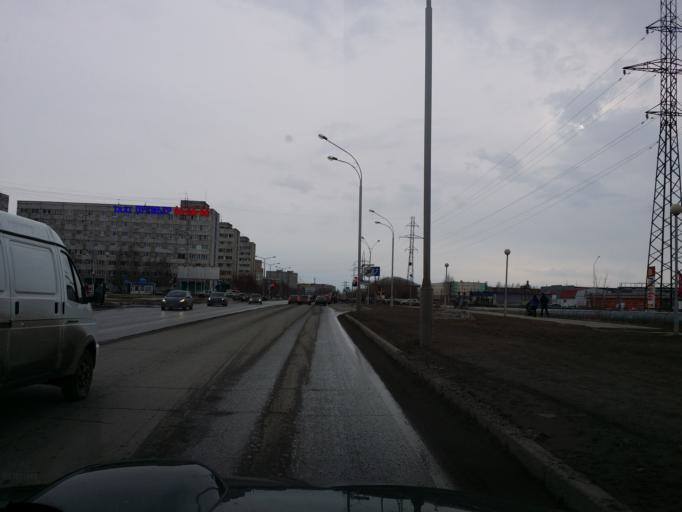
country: RU
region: Khanty-Mansiyskiy Avtonomnyy Okrug
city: Nizhnevartovsk
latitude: 60.9515
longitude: 76.5639
